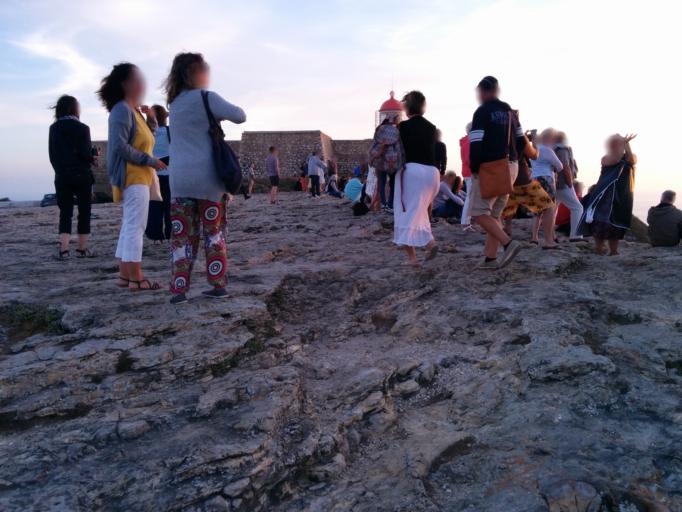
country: PT
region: Faro
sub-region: Vila do Bispo
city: Sagres
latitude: 37.0238
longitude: -8.9956
